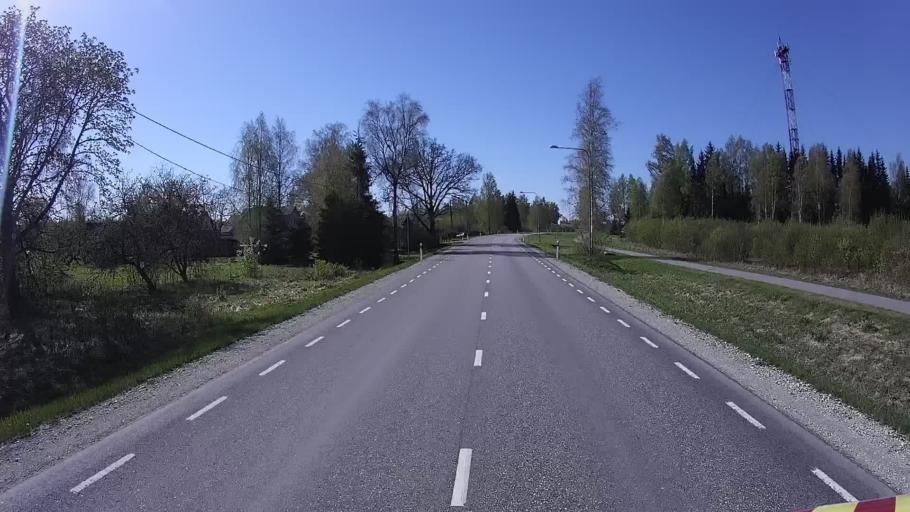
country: EE
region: Raplamaa
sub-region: Jaervakandi vald
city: Jarvakandi
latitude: 58.7854
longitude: 24.8188
